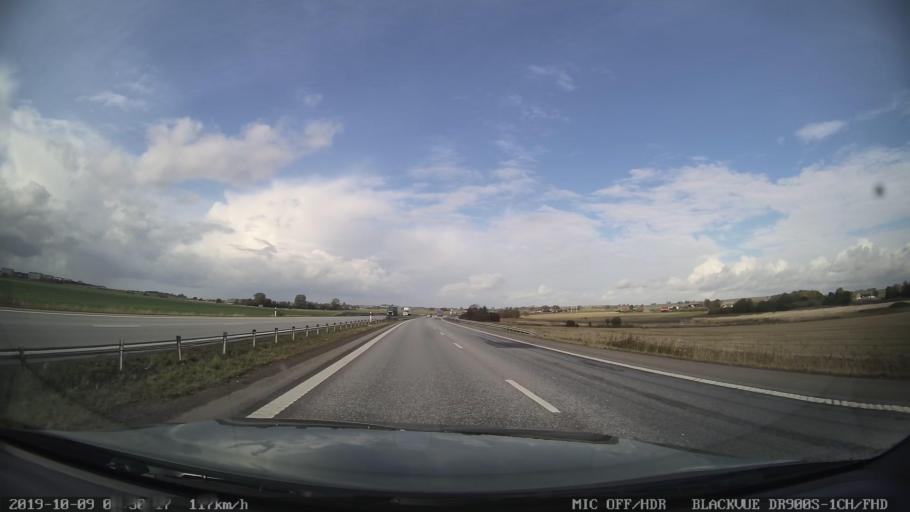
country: SE
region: Skane
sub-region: Landskrona
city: Landskrona
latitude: 55.8900
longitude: 12.8716
